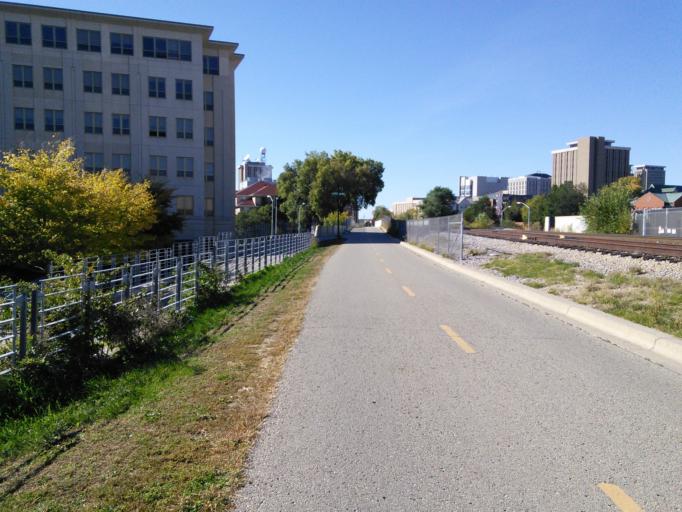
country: US
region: Wisconsin
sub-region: Dane County
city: Madison
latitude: 43.0694
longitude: -89.3998
